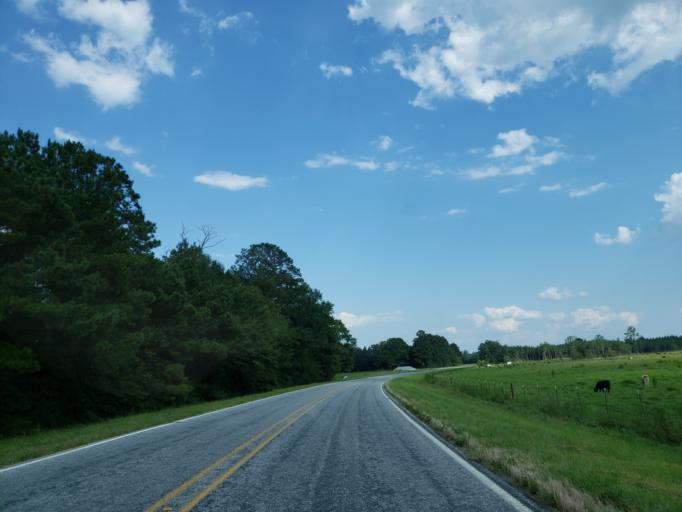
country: US
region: Mississippi
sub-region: Jones County
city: Ellisville
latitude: 31.6230
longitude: -89.3591
